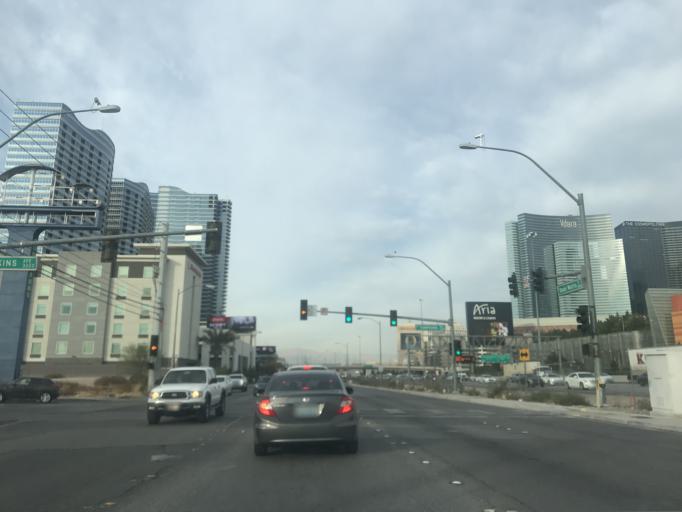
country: US
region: Nevada
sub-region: Clark County
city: Paradise
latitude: 36.1043
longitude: -115.1813
